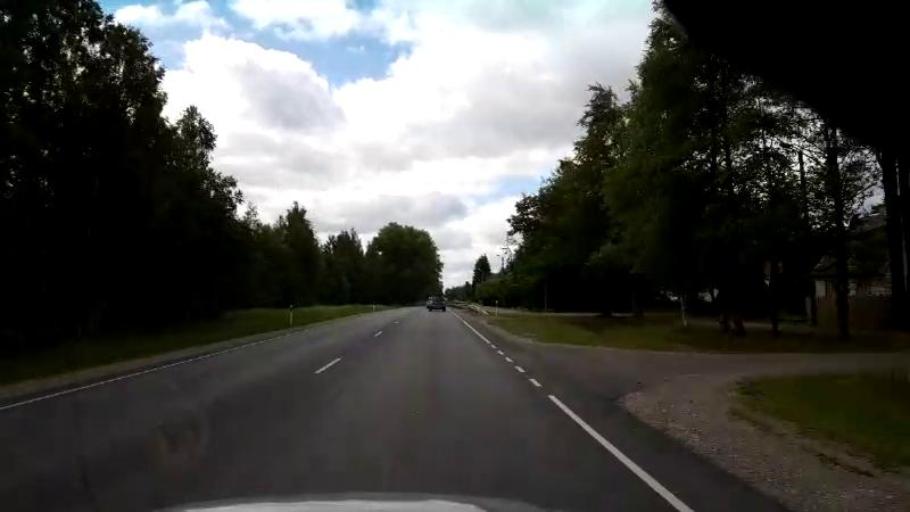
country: EE
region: Paernumaa
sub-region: Sauga vald
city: Sauga
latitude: 58.4187
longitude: 24.4944
